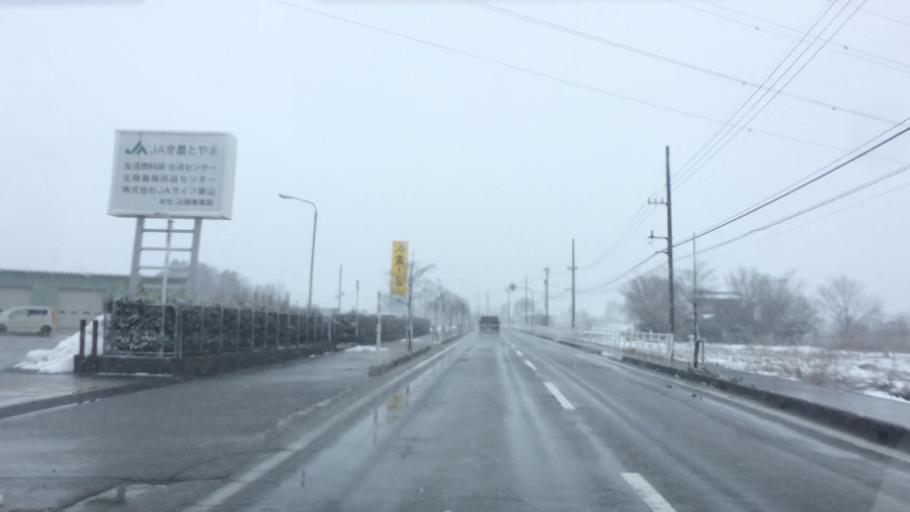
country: JP
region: Toyama
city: Toyama-shi
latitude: 36.6304
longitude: 137.2233
